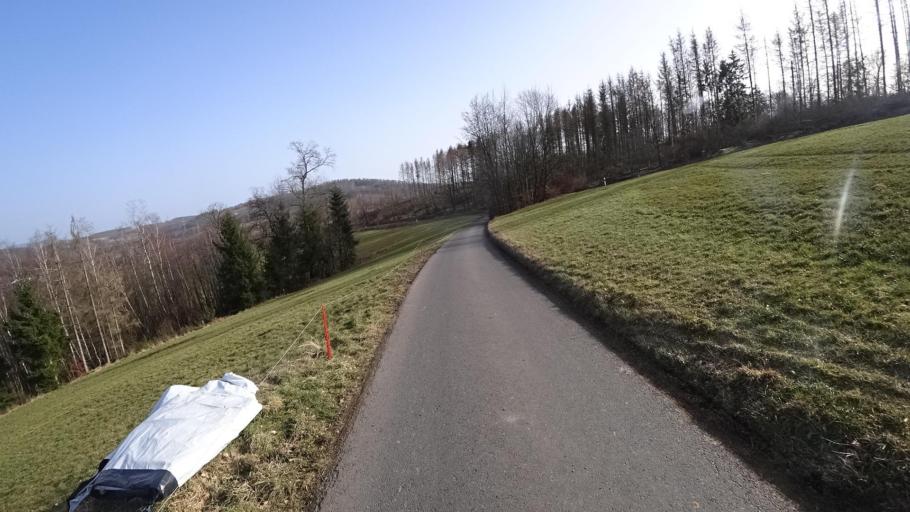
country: DE
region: Rheinland-Pfalz
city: Mittelhof
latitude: 50.7747
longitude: 7.7951
